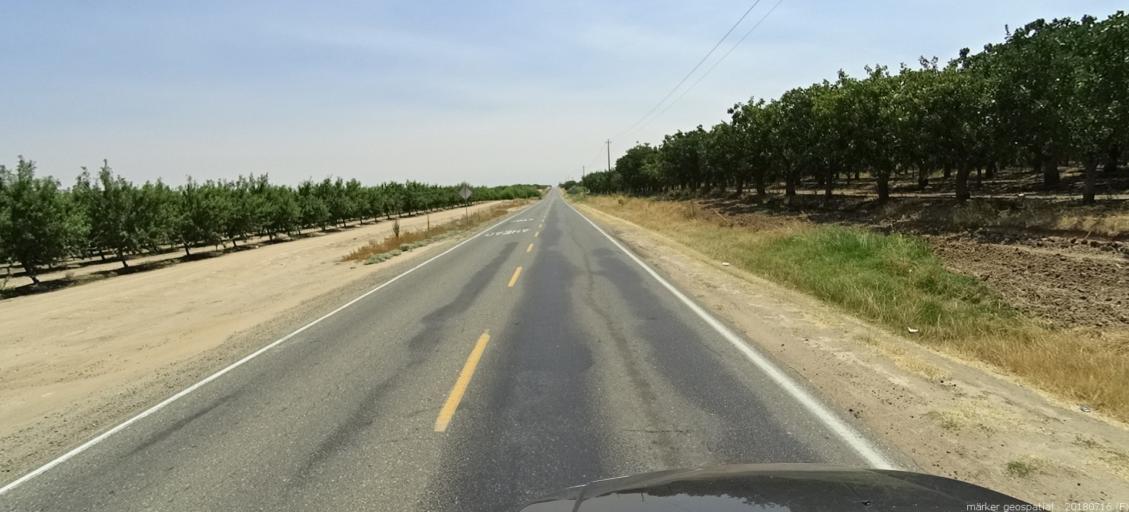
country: US
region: California
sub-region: Madera County
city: Madera Acres
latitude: 37.0544
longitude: -120.0727
